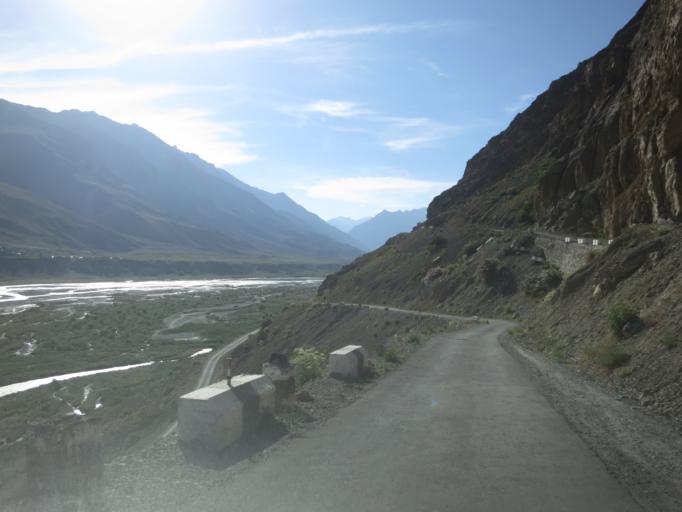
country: IN
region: Himachal Pradesh
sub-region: Shimla
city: Sarahan
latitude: 32.2555
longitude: 78.0464
